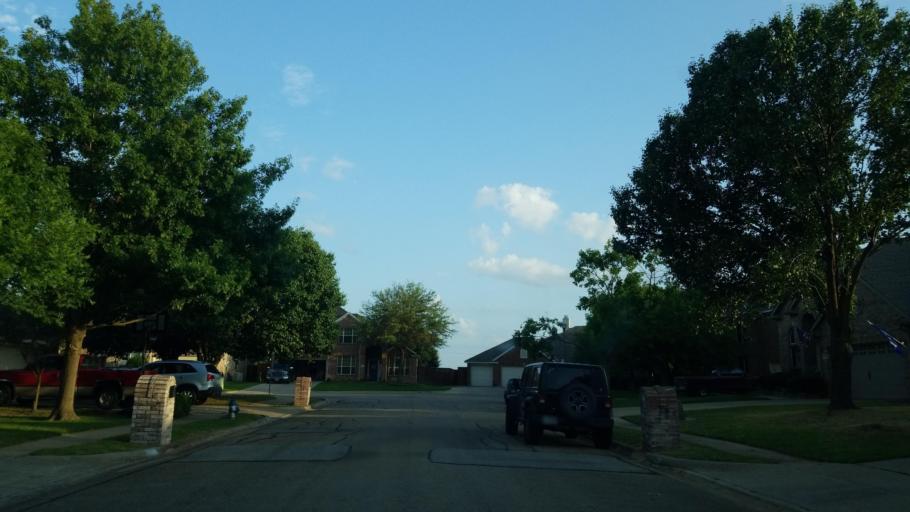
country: US
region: Texas
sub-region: Denton County
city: Copper Canyon
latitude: 33.1482
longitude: -97.1266
